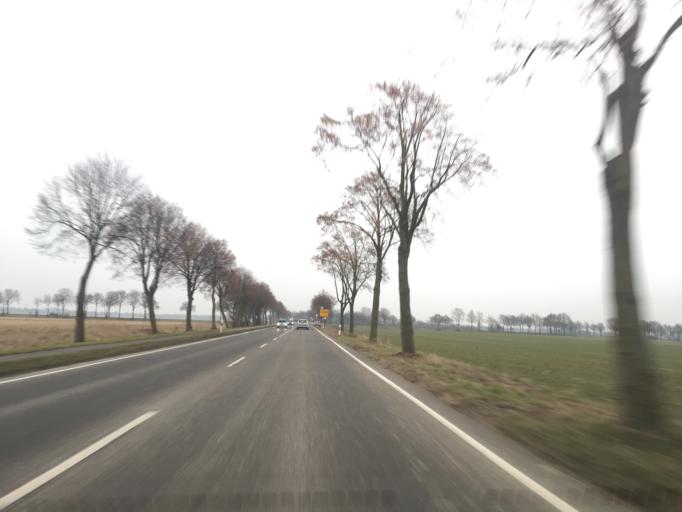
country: DE
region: North Rhine-Westphalia
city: Erkelenz
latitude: 51.0910
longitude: 6.2716
